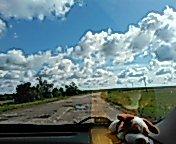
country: RU
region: Penza
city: Mokshan
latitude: 53.3796
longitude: 44.2548
